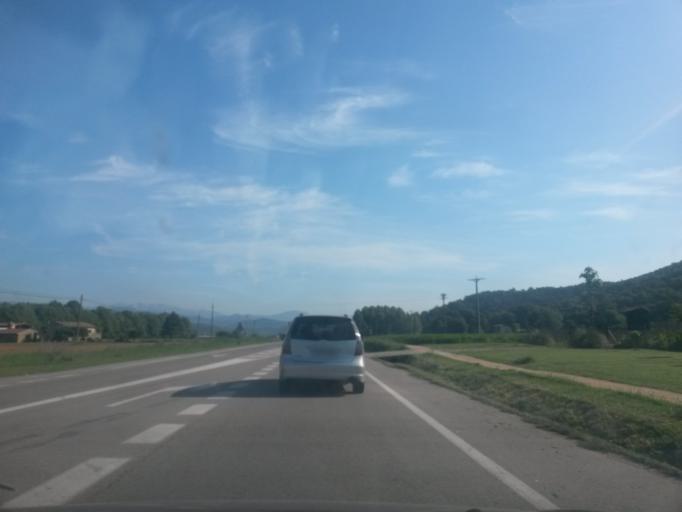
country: ES
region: Catalonia
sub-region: Provincia de Girona
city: Bas
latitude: 42.1307
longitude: 2.4511
